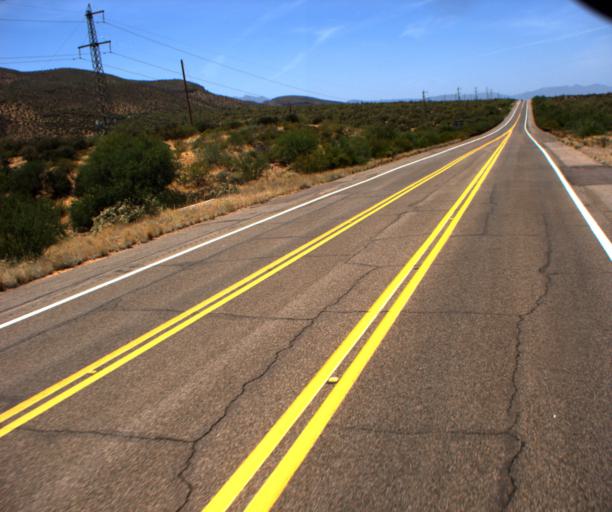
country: US
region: Arizona
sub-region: Gila County
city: Tonto Basin
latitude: 33.6491
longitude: -111.0968
